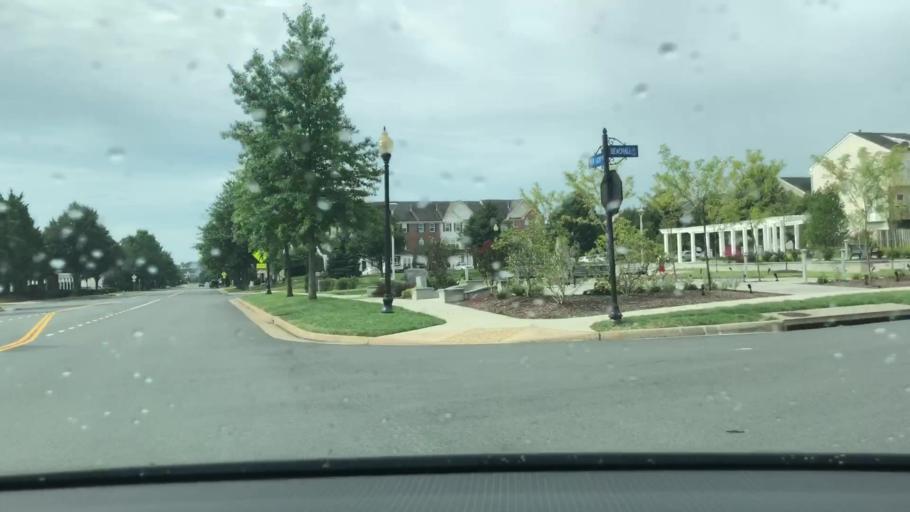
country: US
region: Virginia
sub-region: Loudoun County
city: South Riding
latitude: 38.9146
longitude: -77.5138
